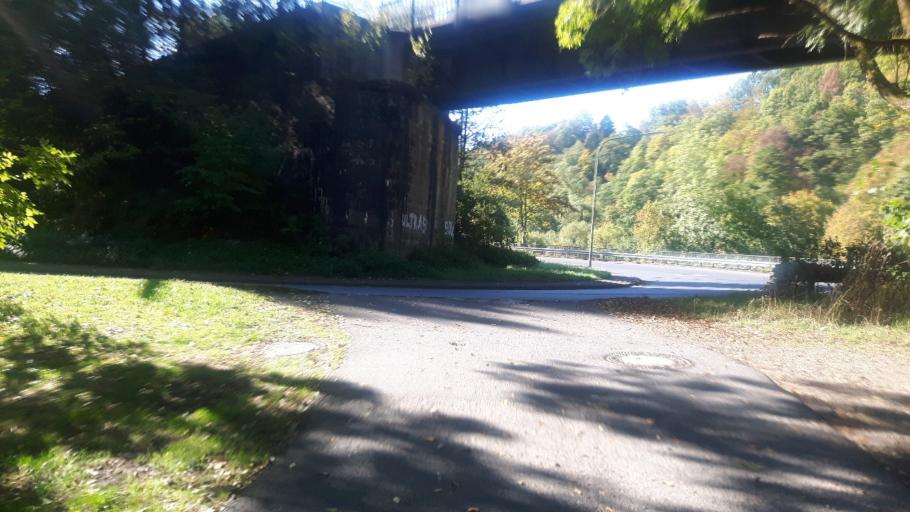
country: DE
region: Rheinland-Pfalz
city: Niederirsen
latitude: 50.8019
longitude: 7.6056
